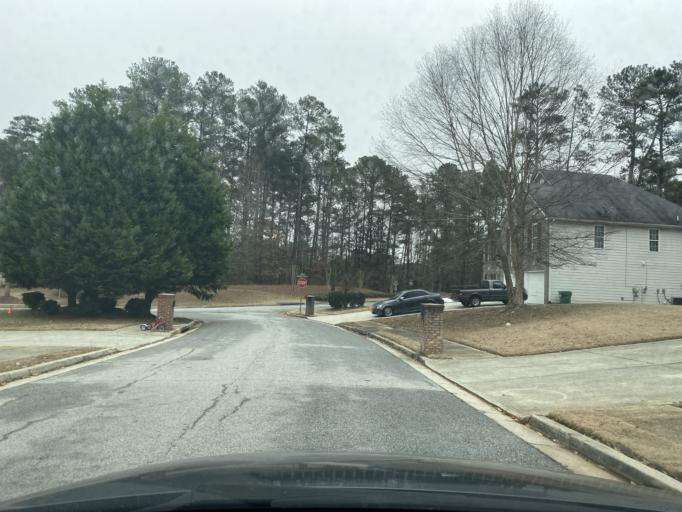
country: US
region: Georgia
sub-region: DeKalb County
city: Pine Mountain
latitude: 33.6870
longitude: -84.1440
